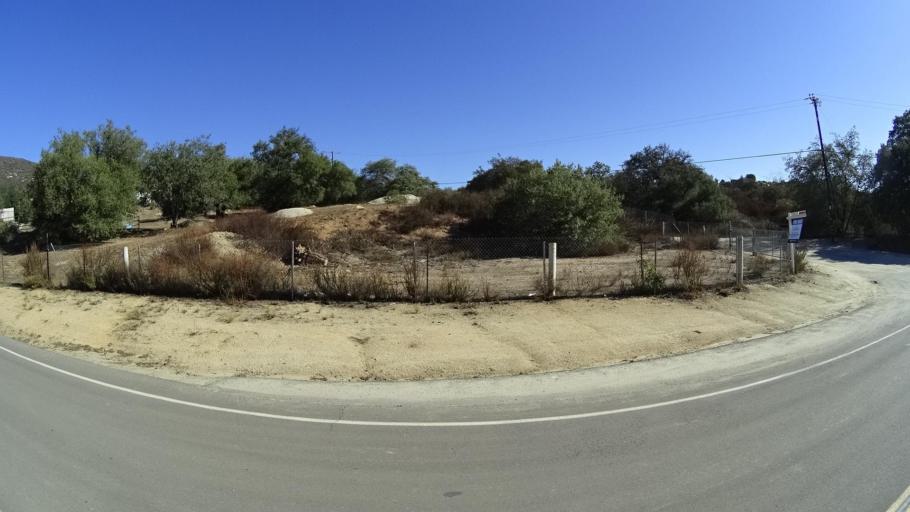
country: MX
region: Baja California
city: Tecate
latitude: 32.6734
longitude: -116.7087
